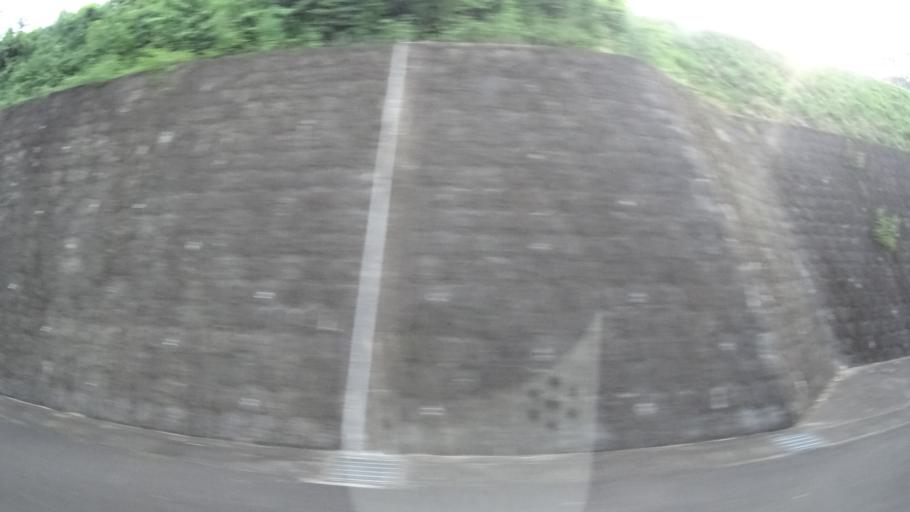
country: JP
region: Tochigi
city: Karasuyama
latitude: 36.6182
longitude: 140.1550
